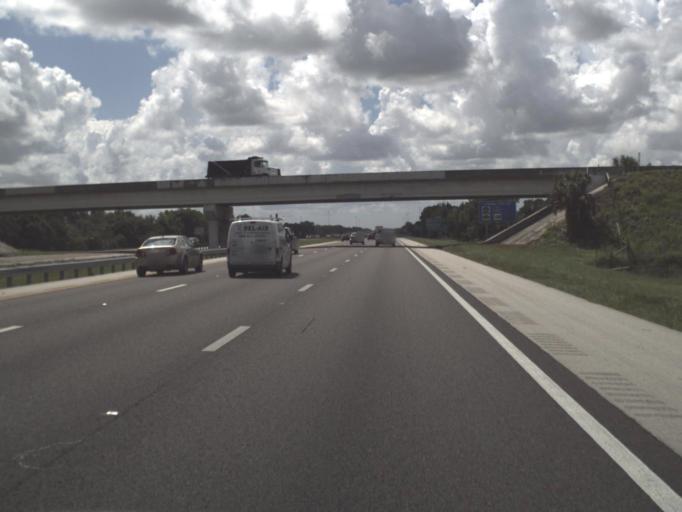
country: US
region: Florida
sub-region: Lee County
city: Bonita Springs
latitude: 26.3469
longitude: -81.7537
